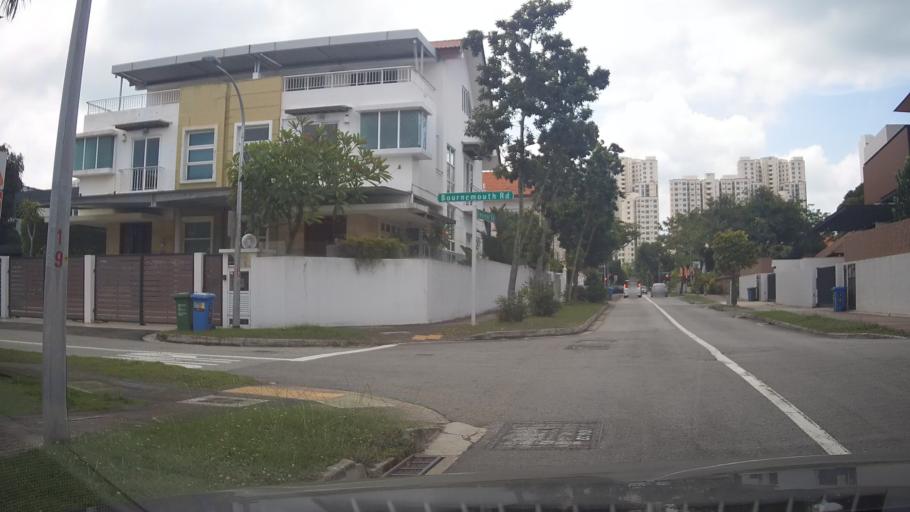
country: SG
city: Singapore
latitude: 1.3021
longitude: 103.8935
